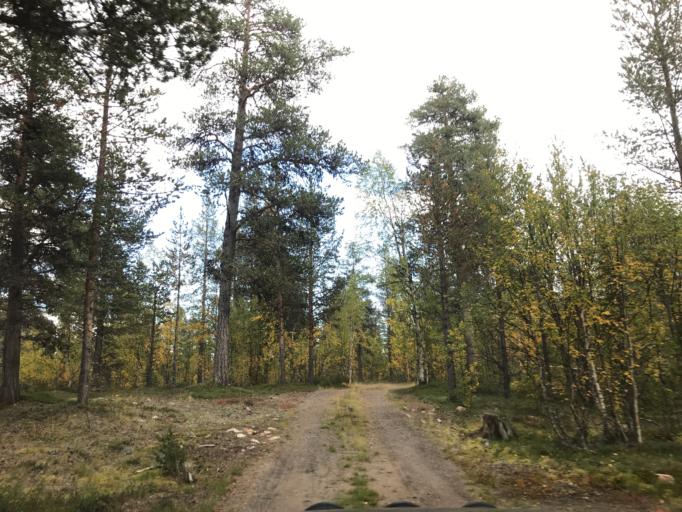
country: SE
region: Norrbotten
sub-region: Gallivare Kommun
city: Malmberget
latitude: 67.5851
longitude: 20.8480
